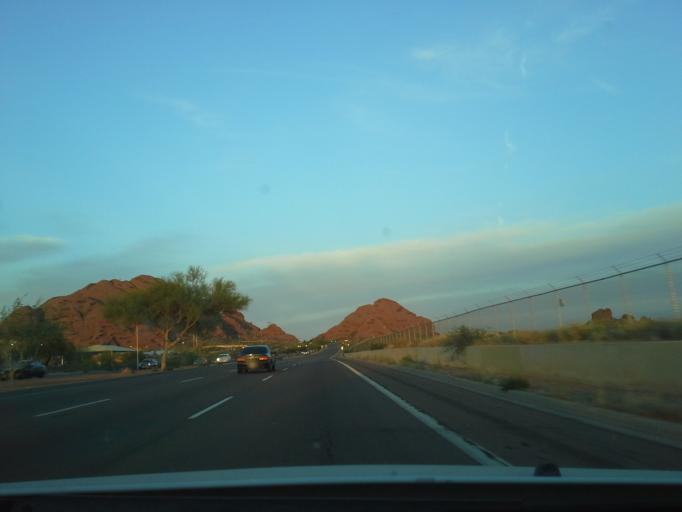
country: US
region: Arizona
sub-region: Maricopa County
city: Tempe Junction
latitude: 33.4654
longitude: -111.9682
